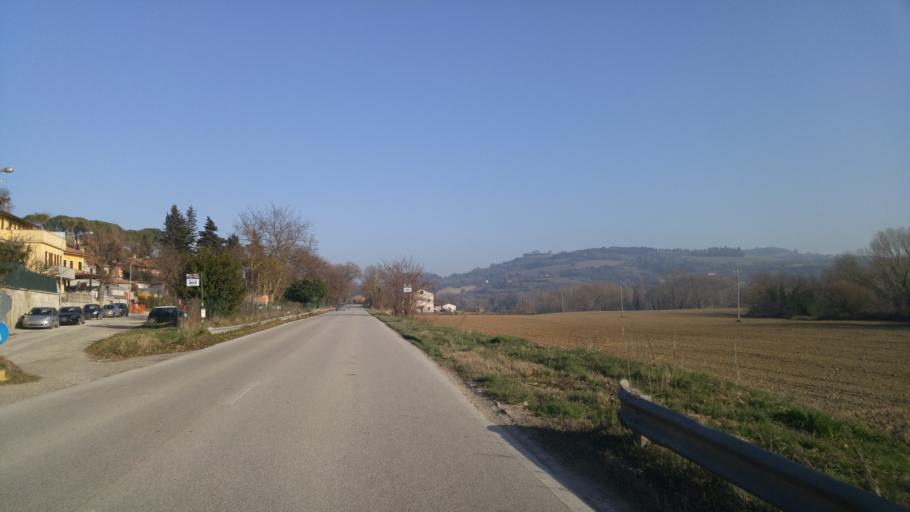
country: IT
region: The Marches
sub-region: Provincia di Pesaro e Urbino
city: Fenile
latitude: 43.8372
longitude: 12.9443
